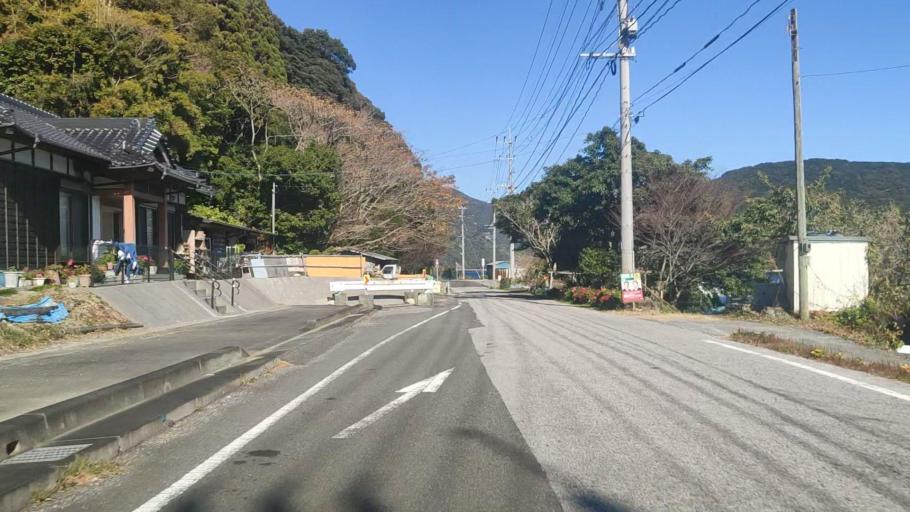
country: JP
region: Oita
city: Saiki
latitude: 32.8301
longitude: 131.9595
